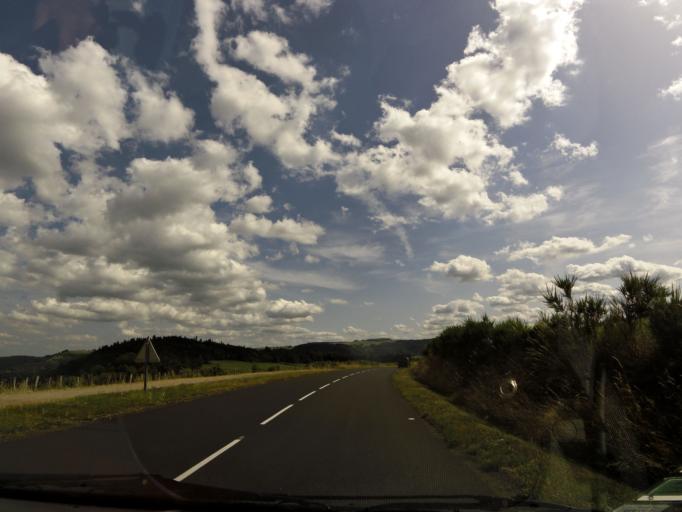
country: FR
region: Auvergne
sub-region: Departement du Puy-de-Dome
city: Aydat
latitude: 45.5369
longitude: 2.9485
